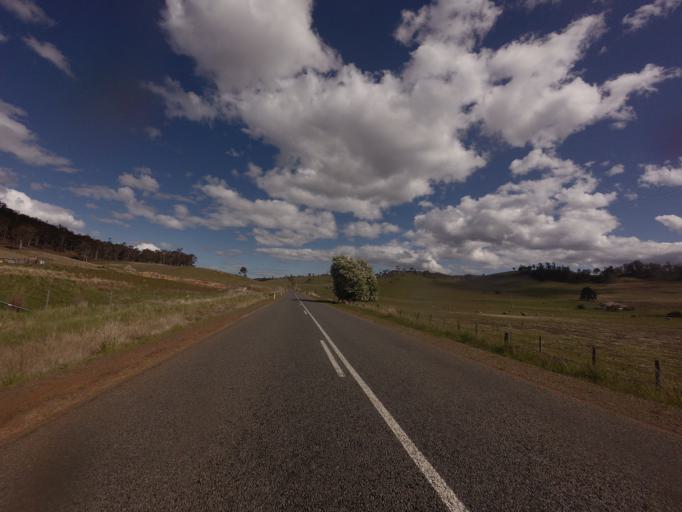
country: AU
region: Tasmania
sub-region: Brighton
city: Bridgewater
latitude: -42.4813
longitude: 147.3271
